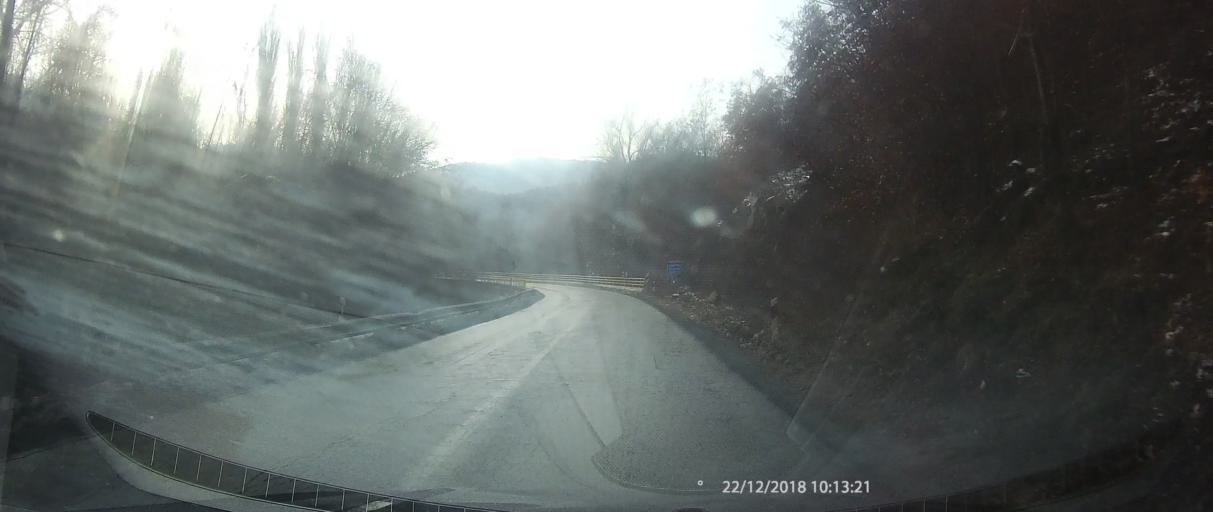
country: MK
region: Kratovo
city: Kratovo
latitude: 42.1740
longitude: 22.2239
